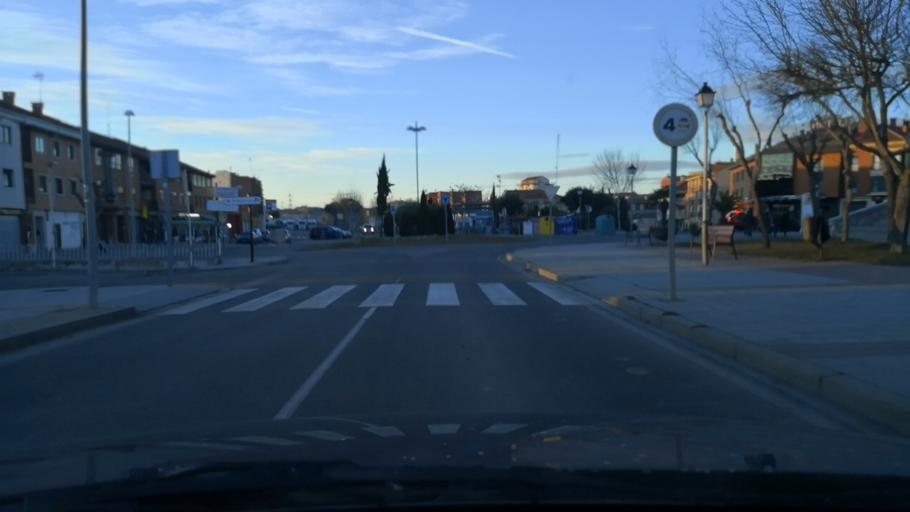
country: ES
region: Castille and Leon
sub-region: Provincia de Valladolid
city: Tordesillas
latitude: 41.5013
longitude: -5.0041
